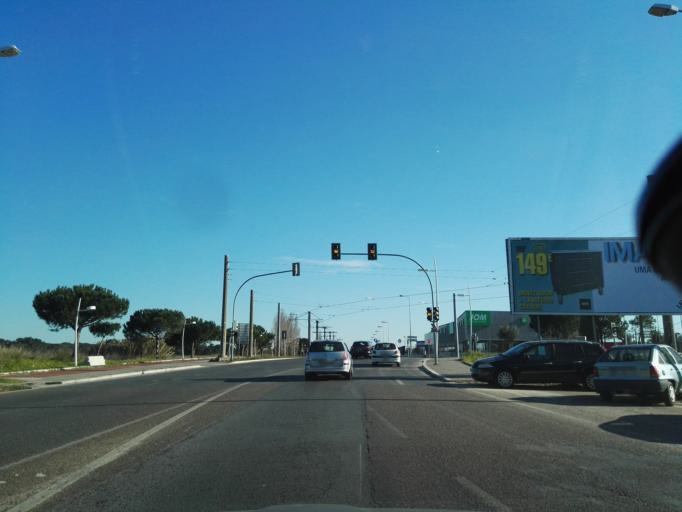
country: PT
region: Setubal
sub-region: Seixal
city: Corroios
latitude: 38.6382
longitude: -9.1484
